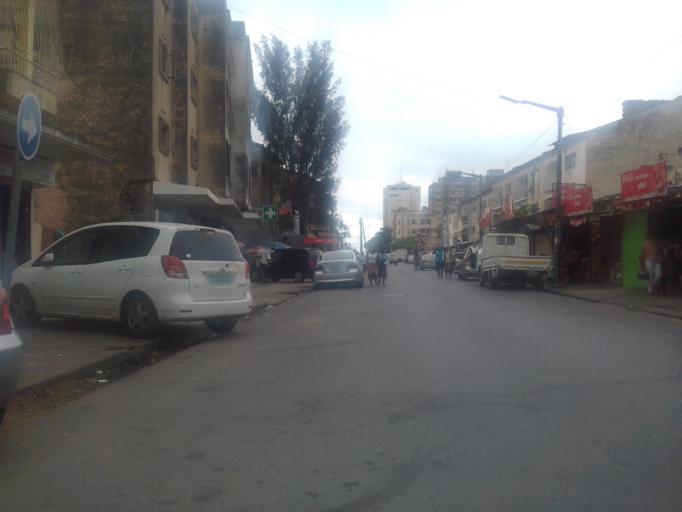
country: MZ
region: Maputo City
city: Maputo
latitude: -25.9539
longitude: 32.5856
